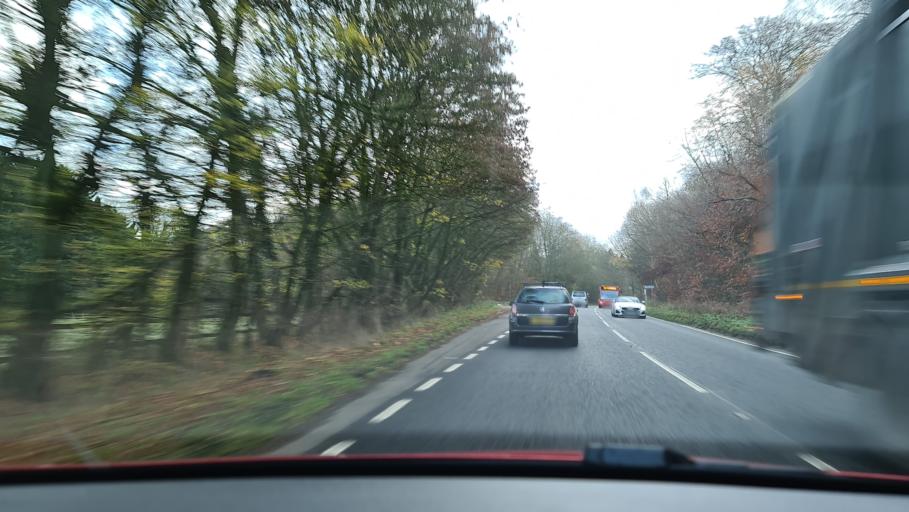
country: GB
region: England
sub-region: Buckinghamshire
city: Amersham
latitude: 51.6614
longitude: -0.6673
